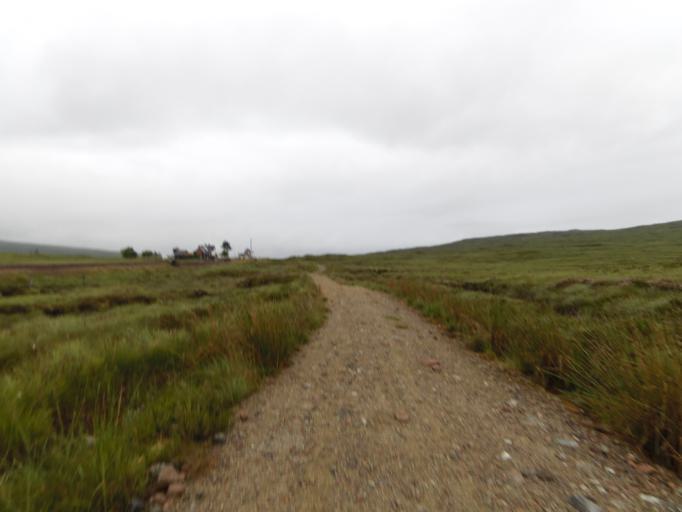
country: GB
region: Scotland
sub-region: Highland
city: Spean Bridge
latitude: 56.7615
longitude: -4.6935
